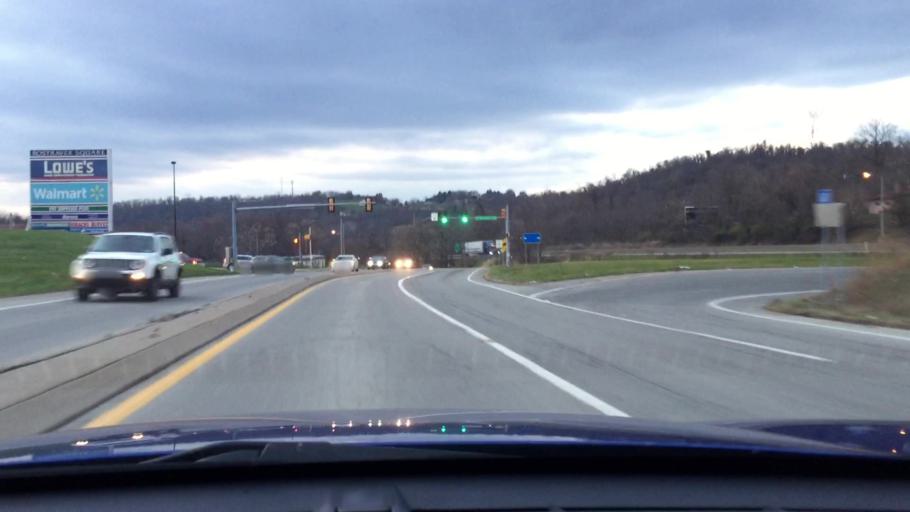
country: US
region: Pennsylvania
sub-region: Westmoreland County
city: Lynnwood-Pricedale
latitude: 40.1395
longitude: -79.8458
